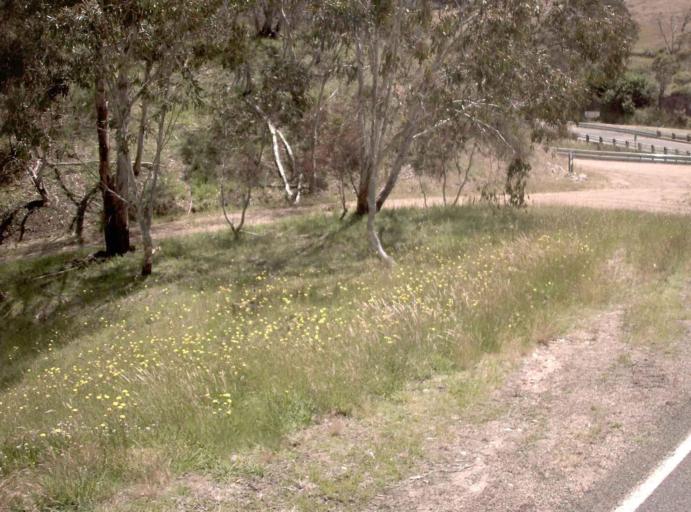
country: AU
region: Victoria
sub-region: Alpine
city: Mount Beauty
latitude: -37.1125
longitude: 147.5774
